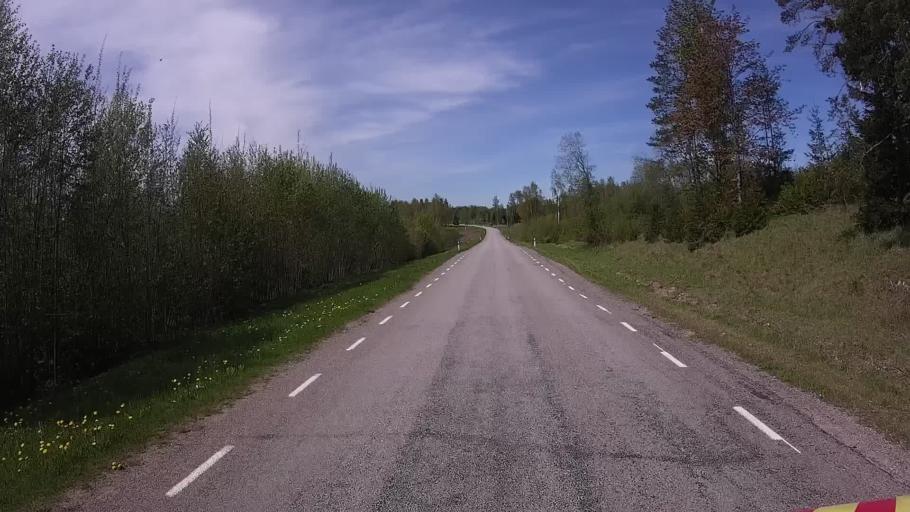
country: EE
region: Vorumaa
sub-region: Antsla vald
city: Vana-Antsla
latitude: 57.6399
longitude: 26.3318
